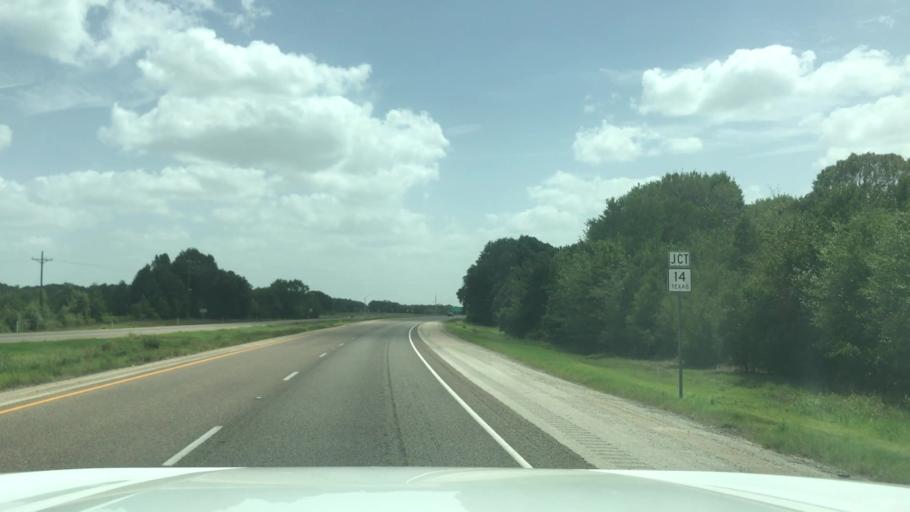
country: US
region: Texas
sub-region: Robertson County
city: Calvert
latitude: 31.1186
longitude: -96.7121
